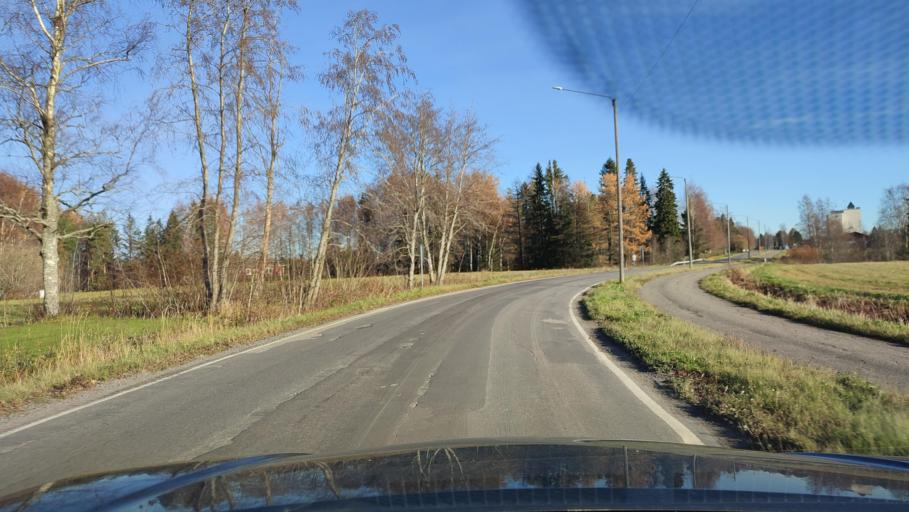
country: FI
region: Southern Ostrobothnia
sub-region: Suupohja
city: Teuva
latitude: 62.4731
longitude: 21.7313
